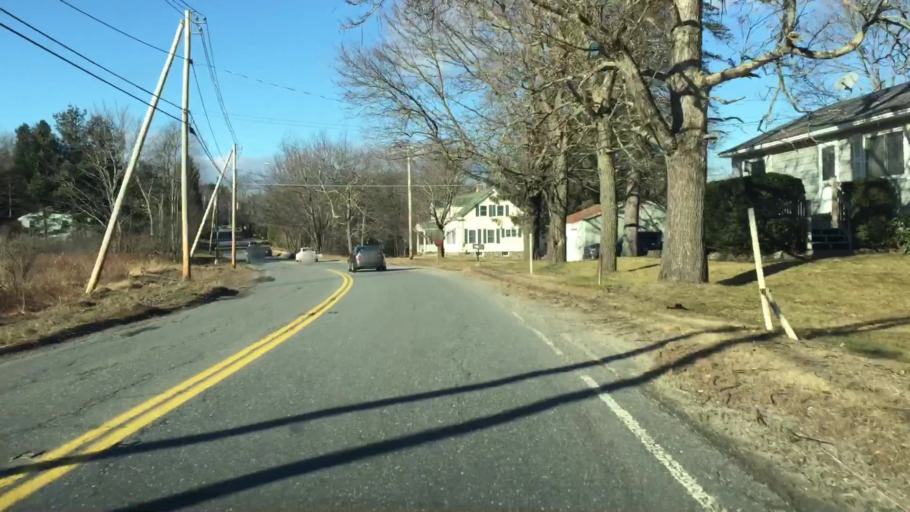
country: US
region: Massachusetts
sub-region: Worcester County
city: Sterling
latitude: 42.4151
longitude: -71.8019
